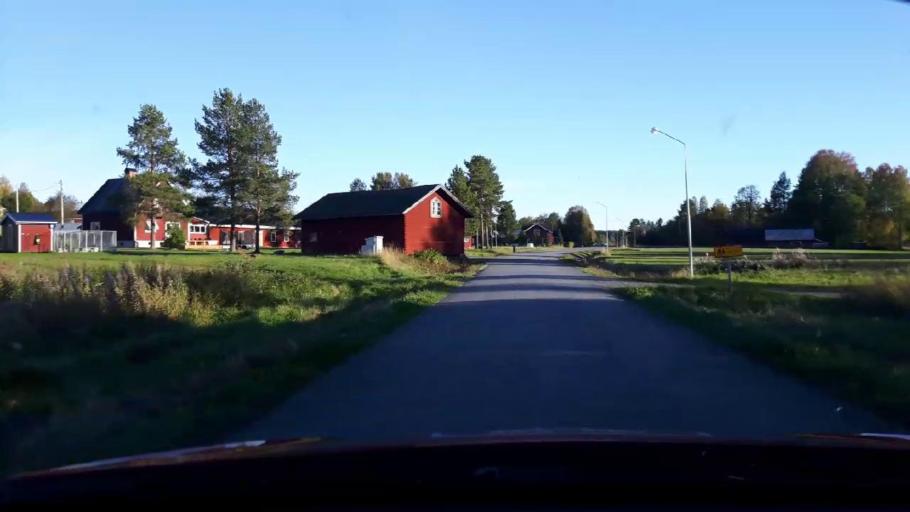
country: SE
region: Jaemtland
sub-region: OEstersunds Kommun
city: Lit
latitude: 63.6154
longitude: 14.7698
